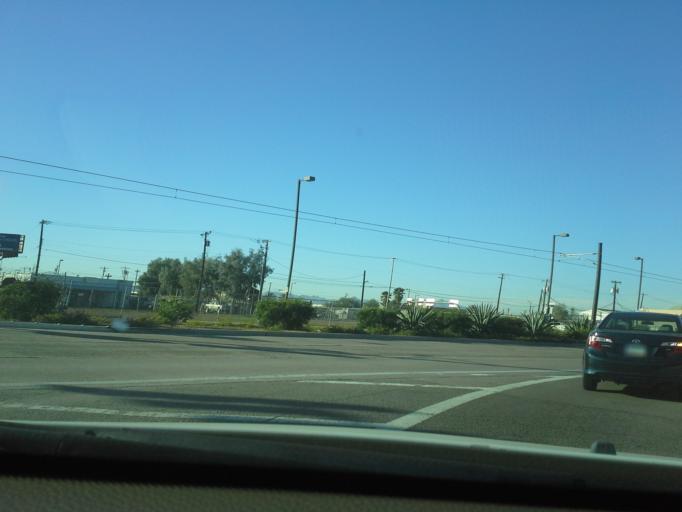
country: US
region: Arizona
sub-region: Maricopa County
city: Phoenix
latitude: 33.4485
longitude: -112.0383
